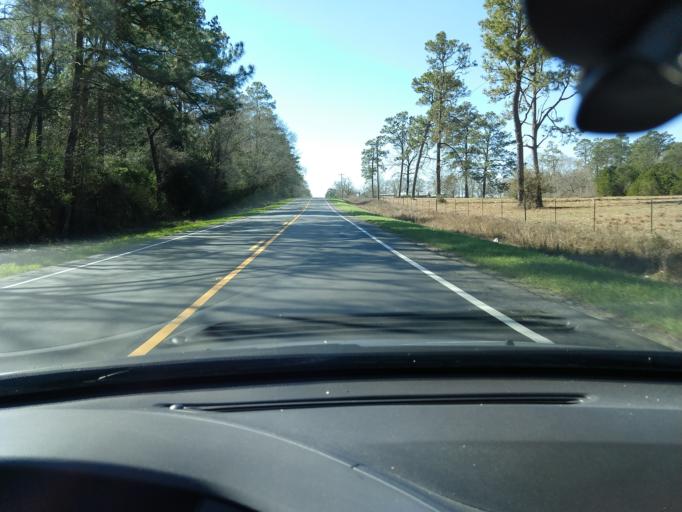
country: US
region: Alabama
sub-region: Covington County
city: Andalusia
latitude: 31.1963
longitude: -86.5613
